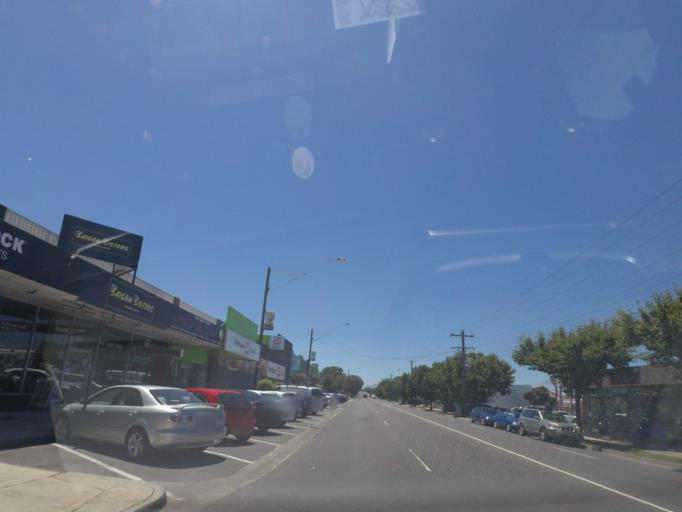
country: AU
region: Victoria
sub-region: Whittlesea
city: Thomastown
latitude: -37.6783
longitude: 145.0142
